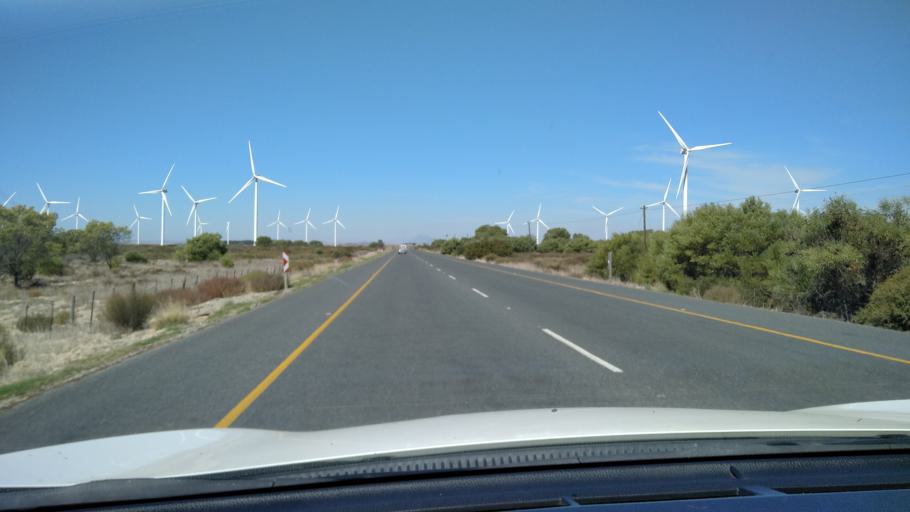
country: ZA
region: Western Cape
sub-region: West Coast District Municipality
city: Moorreesburg
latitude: -33.0793
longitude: 18.3868
